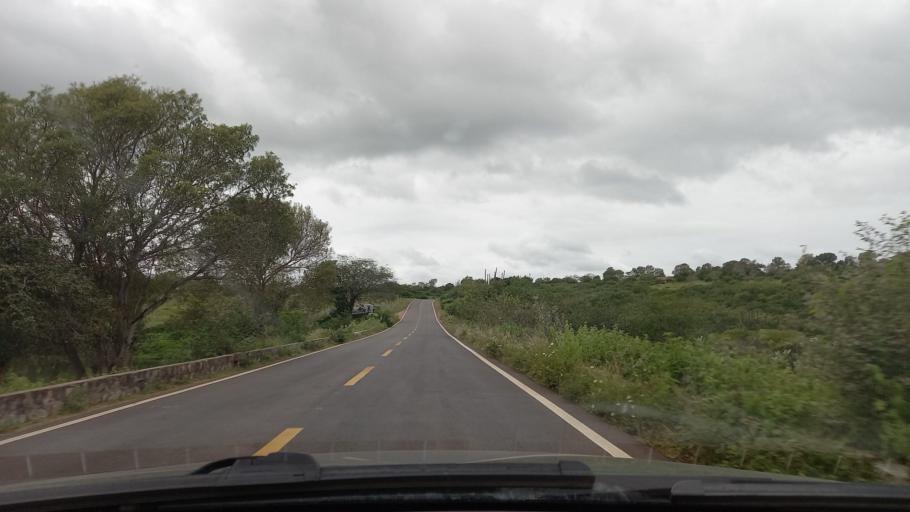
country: BR
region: Sergipe
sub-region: Caninde De Sao Francisco
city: Caninde de Sao Francisco
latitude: -9.6161
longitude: -37.7719
